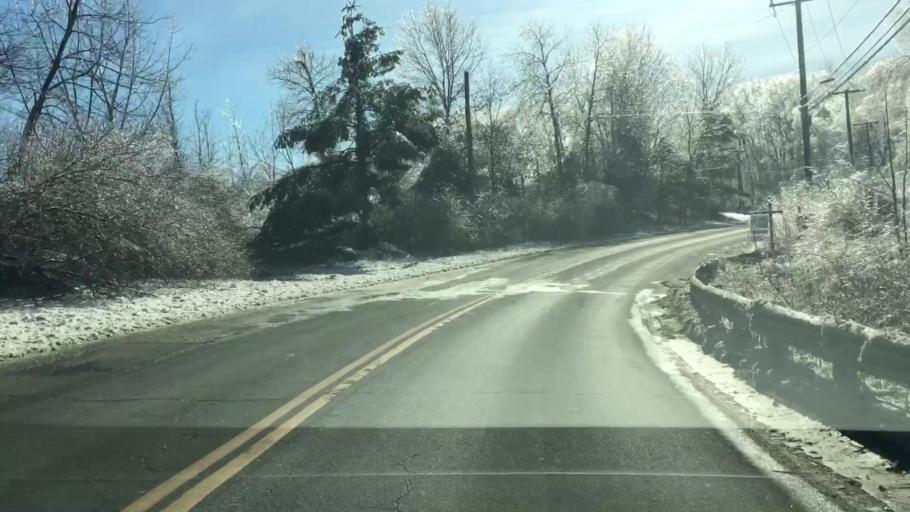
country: US
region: Connecticut
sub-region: Fairfield County
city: Newtown
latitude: 41.4055
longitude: -73.2631
